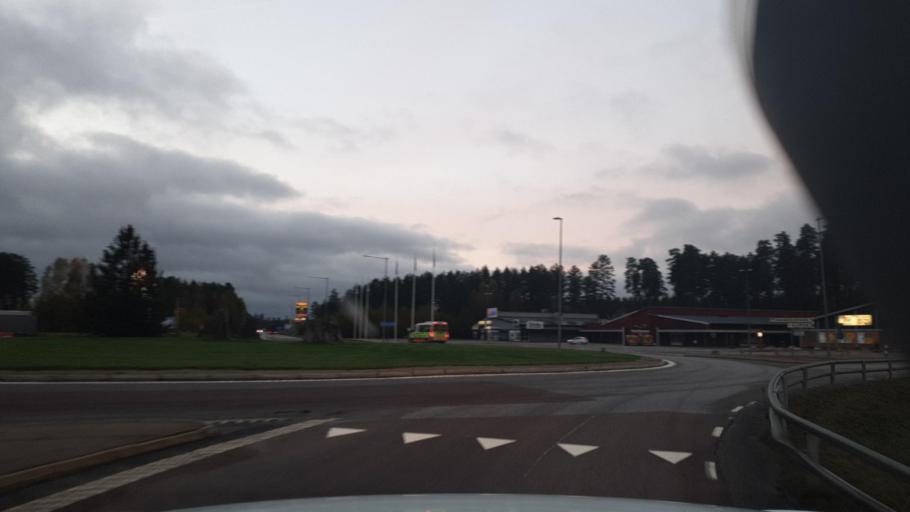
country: SE
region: Vaermland
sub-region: Eda Kommun
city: Charlottenberg
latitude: 59.8797
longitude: 12.2863
